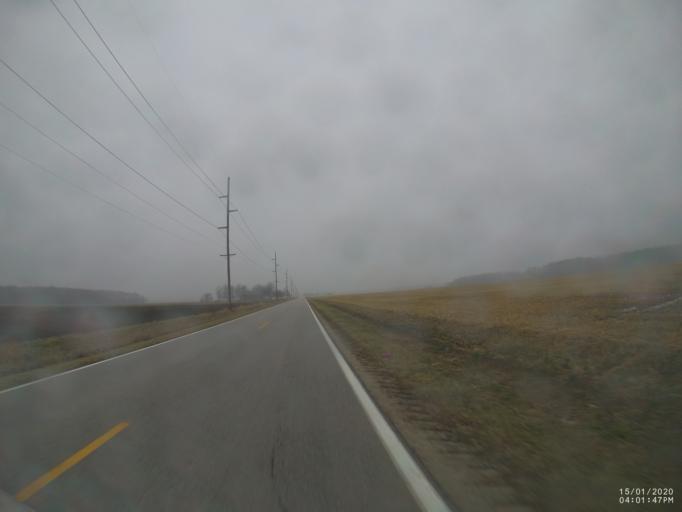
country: US
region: Ohio
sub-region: Sandusky County
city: Woodville
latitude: 41.4137
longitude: -83.3636
